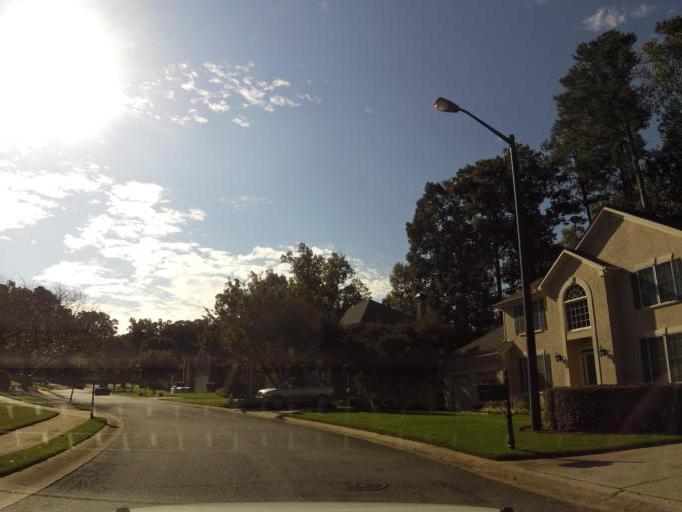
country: US
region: Georgia
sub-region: Cobb County
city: Kennesaw
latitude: 34.0464
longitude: -84.6366
